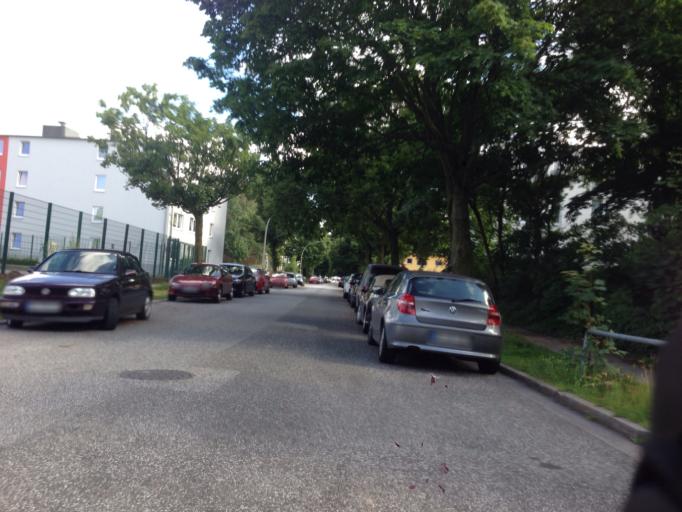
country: DE
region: Hamburg
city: Hamburg
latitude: 53.5788
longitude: 10.0343
